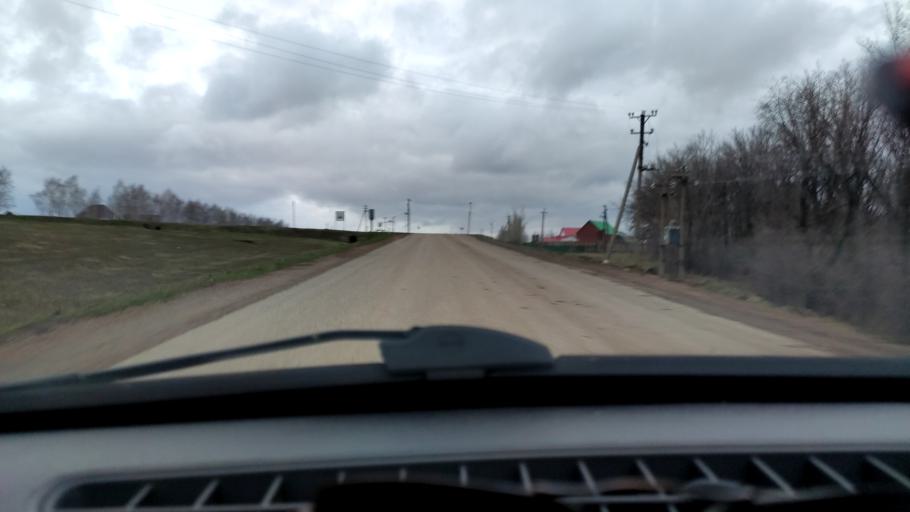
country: RU
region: Bashkortostan
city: Kabakovo
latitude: 54.5237
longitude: 56.1583
